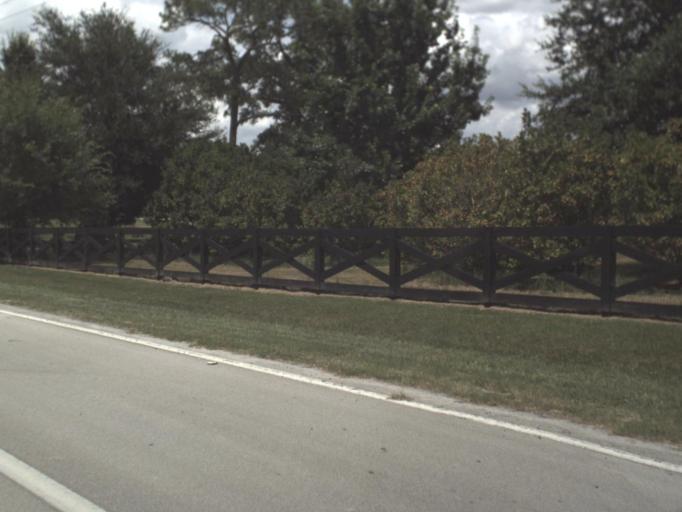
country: US
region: Florida
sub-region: Alachua County
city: High Springs
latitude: 29.8011
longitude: -82.6084
